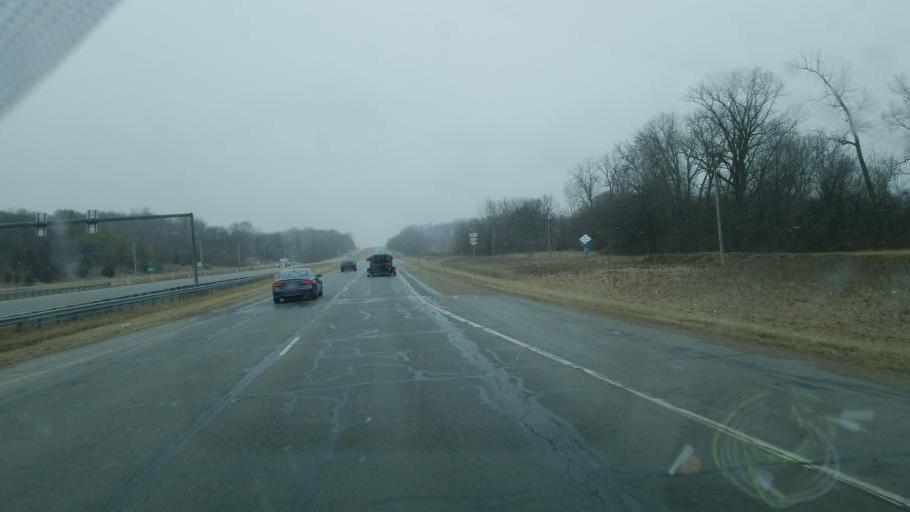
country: US
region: Indiana
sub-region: Miami County
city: Peru
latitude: 40.7799
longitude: -86.0588
